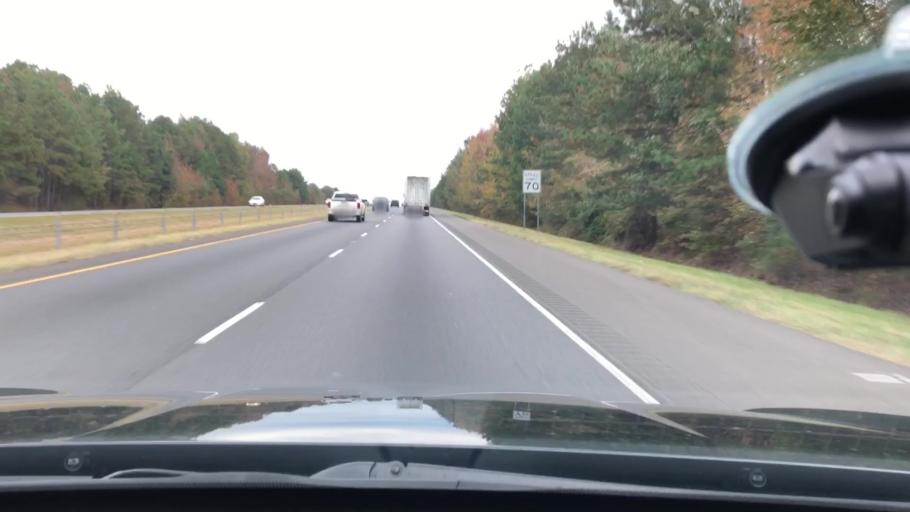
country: US
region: Arkansas
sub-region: Clark County
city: Arkadelphia
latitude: 34.1938
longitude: -93.0590
